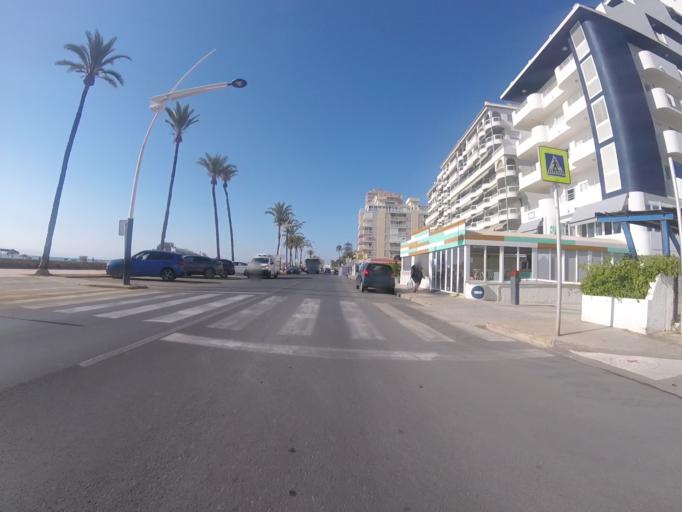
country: ES
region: Valencia
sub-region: Provincia de Castello
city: Peniscola
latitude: 40.3676
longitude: 0.4038
